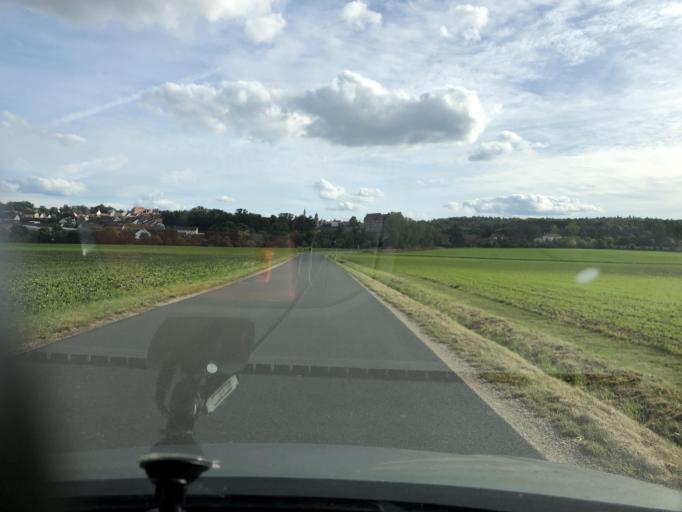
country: DE
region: Bavaria
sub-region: Regierungsbezirk Mittelfranken
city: Cadolzburg
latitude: 49.4673
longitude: 10.8485
